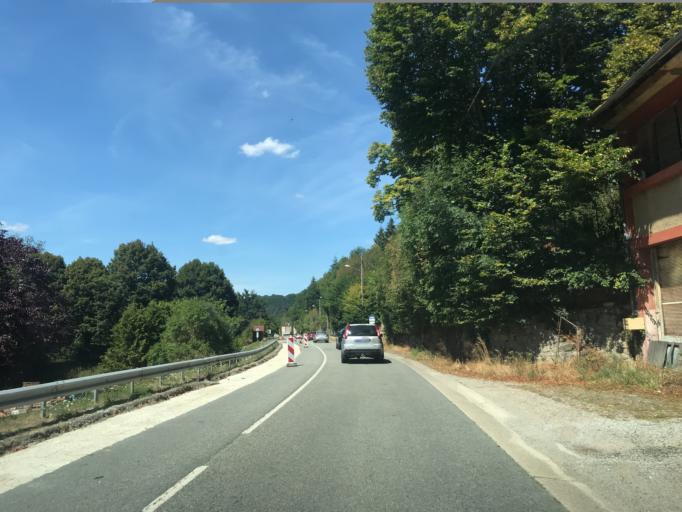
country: FR
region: Limousin
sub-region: Departement de la Creuse
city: Felletin
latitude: 45.9185
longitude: 2.1936
